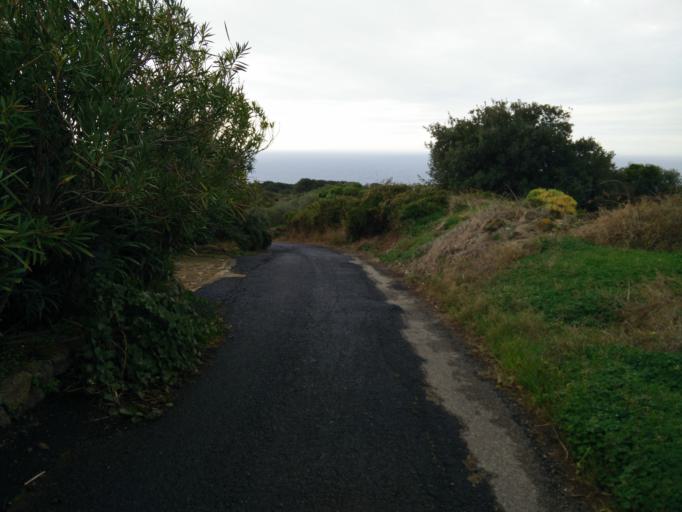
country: IT
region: Sicily
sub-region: Trapani
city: Kamma
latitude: 36.7510
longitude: 11.9978
